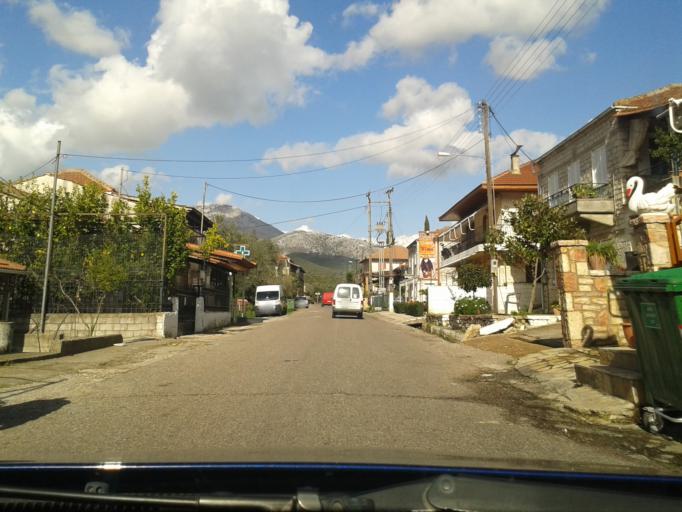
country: GR
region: West Greece
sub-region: Nomos Aitolias kai Akarnanias
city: Astakos
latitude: 38.5946
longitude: 21.0898
